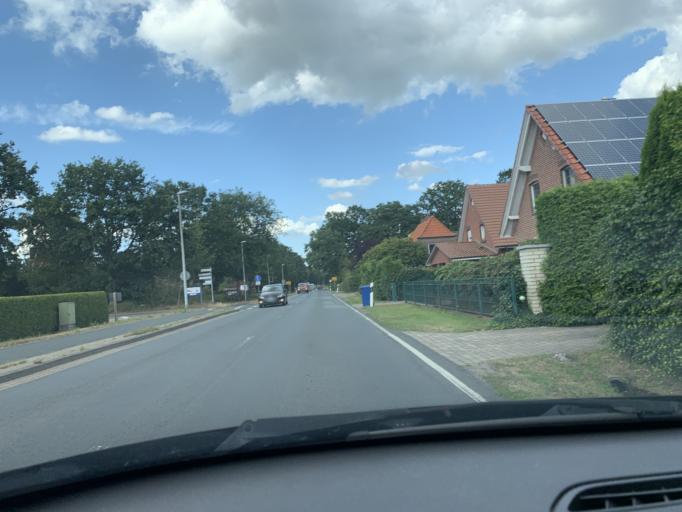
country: DE
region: Lower Saxony
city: Bad Zwischenahn
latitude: 53.1835
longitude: 8.0327
